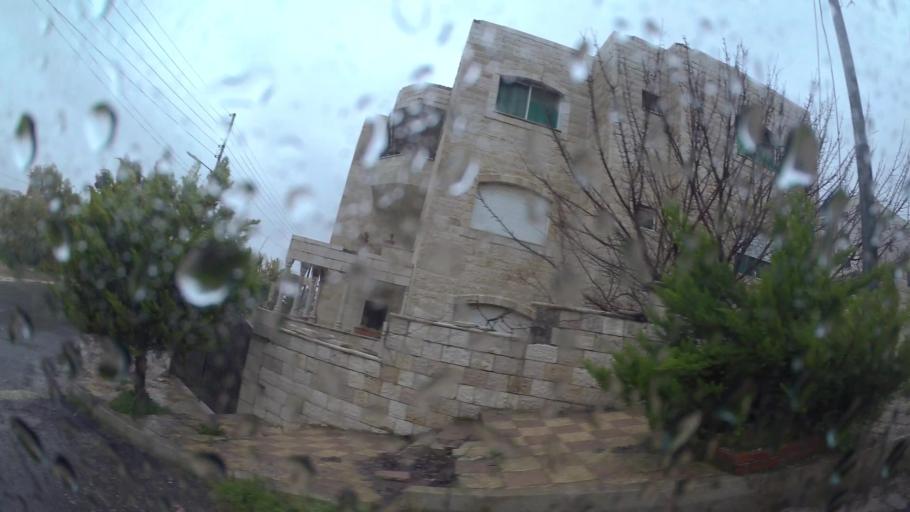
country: JO
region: Amman
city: Al Jubayhah
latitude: 32.0192
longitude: 35.8947
